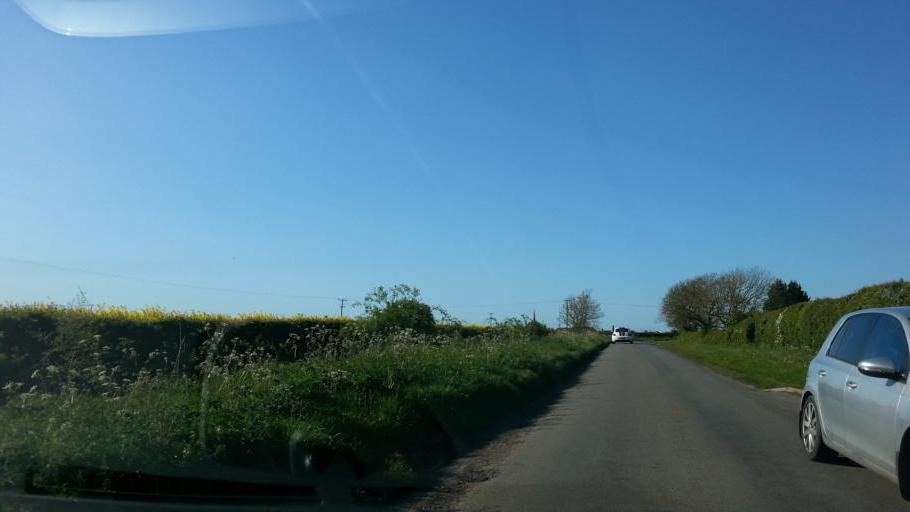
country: GB
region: England
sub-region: Lincolnshire
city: Long Bennington
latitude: 53.0202
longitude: -0.7358
